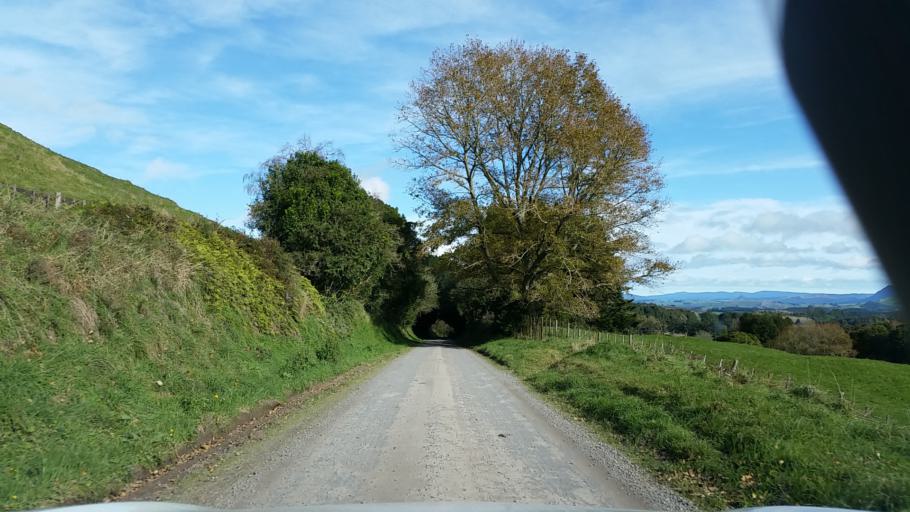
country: NZ
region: Bay of Plenty
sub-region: Rotorua District
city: Rotorua
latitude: -38.2447
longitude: 176.3416
